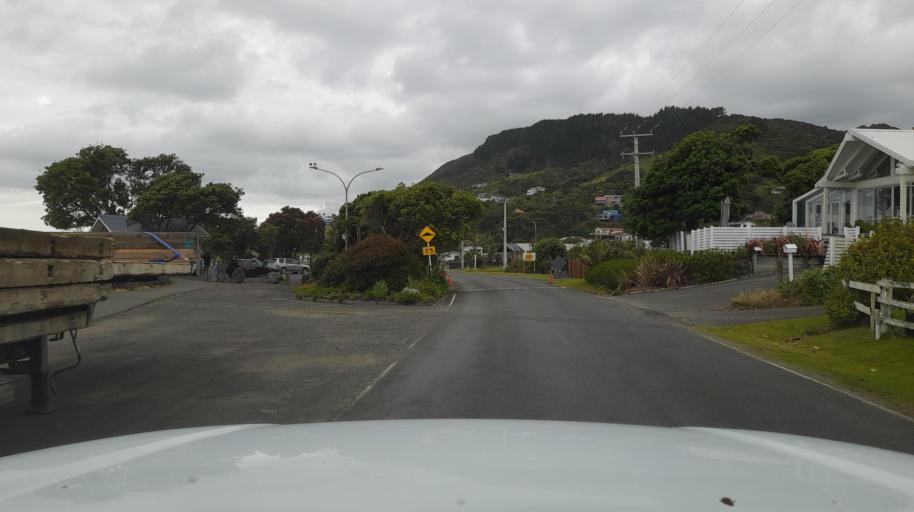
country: NZ
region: Northland
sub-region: Far North District
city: Ahipara
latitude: -35.1781
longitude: 173.1336
